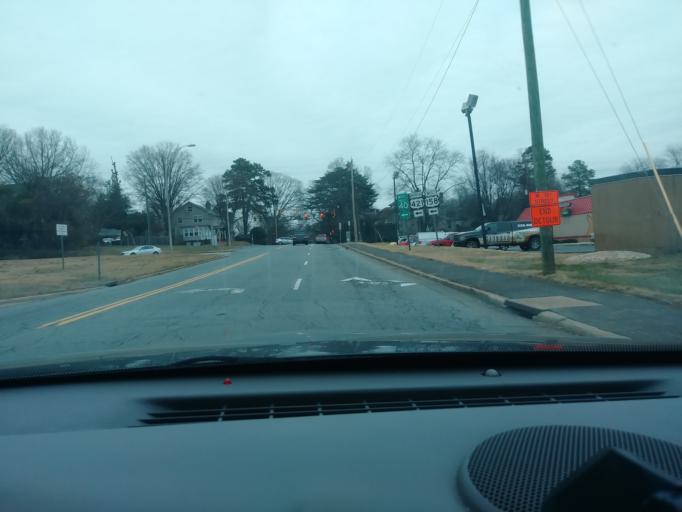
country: US
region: North Carolina
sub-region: Forsyth County
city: Winston-Salem
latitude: 36.0927
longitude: -80.2683
